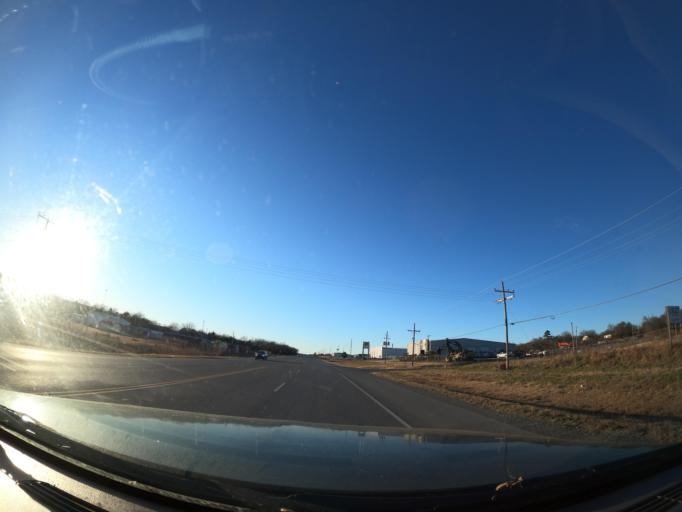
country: US
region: Oklahoma
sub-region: Pittsburg County
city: Krebs
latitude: 34.8968
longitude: -95.6744
